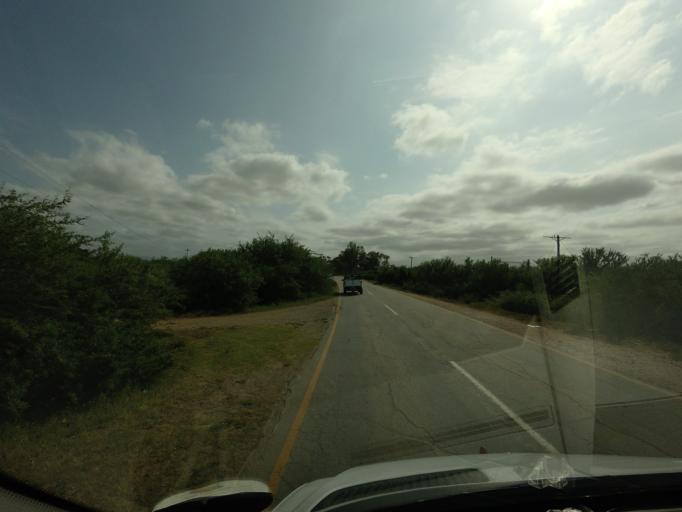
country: ZA
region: Eastern Cape
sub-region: Cacadu District Municipality
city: Kirkwood
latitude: -33.5545
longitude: 25.6888
